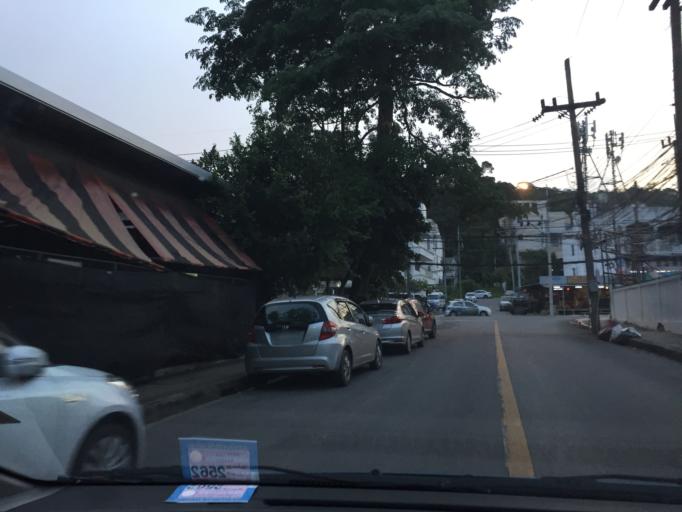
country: TH
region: Phuket
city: Wichit
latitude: 7.8939
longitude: 98.3862
